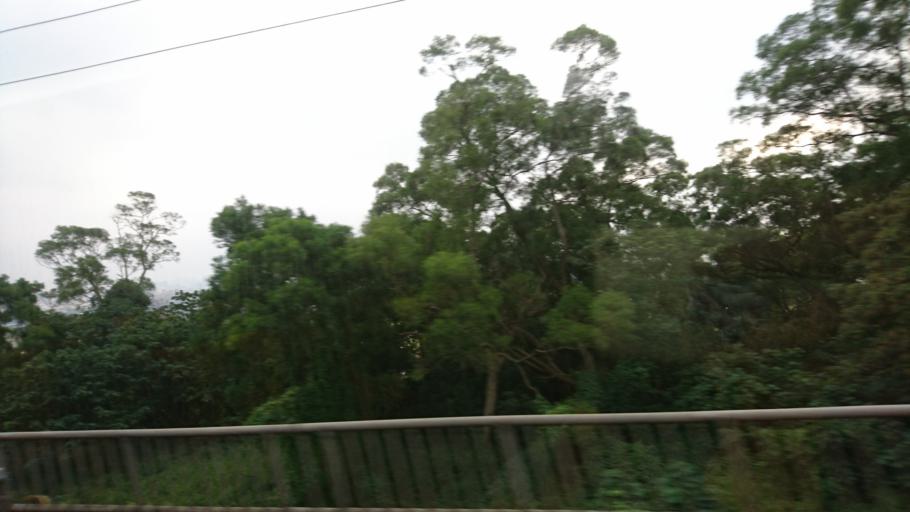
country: TW
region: Taiwan
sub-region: Hsinchu
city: Zhubei
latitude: 24.8592
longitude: 120.9991
